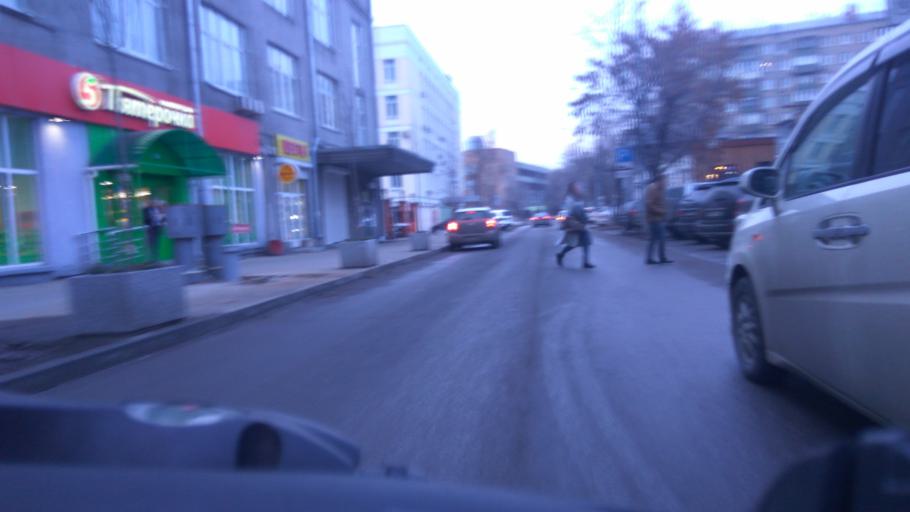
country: RU
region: Moskovskaya
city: Presnenskiy
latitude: 55.7625
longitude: 37.5549
